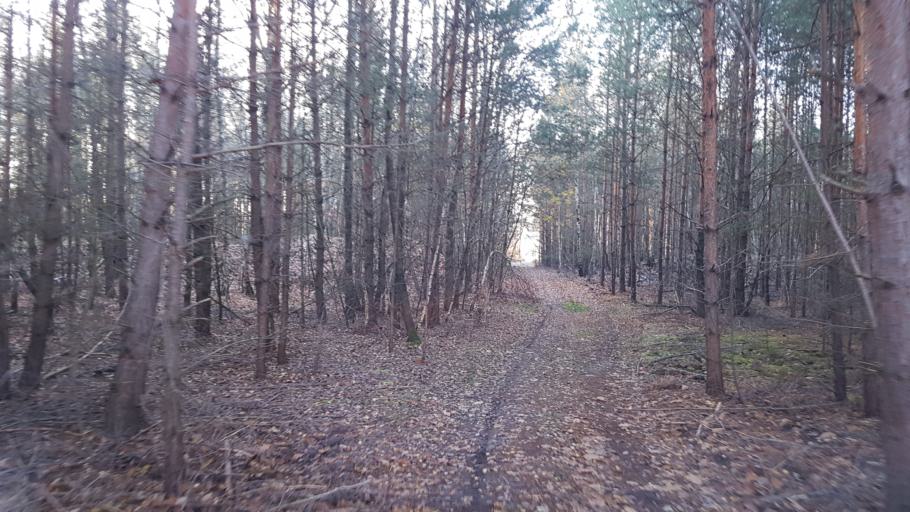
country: DE
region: Brandenburg
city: Sallgast
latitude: 51.5965
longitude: 13.8362
